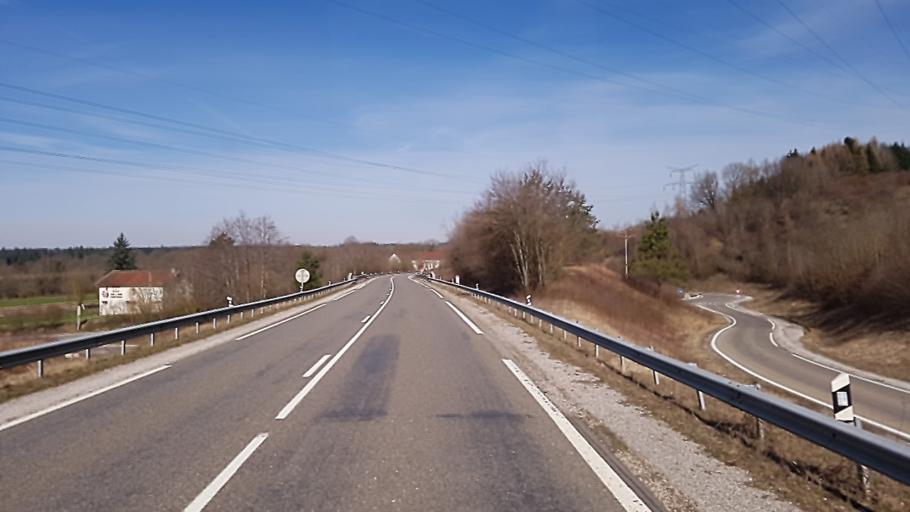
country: FR
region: Franche-Comte
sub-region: Departement du Jura
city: Champagnole
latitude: 46.7594
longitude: 5.9085
